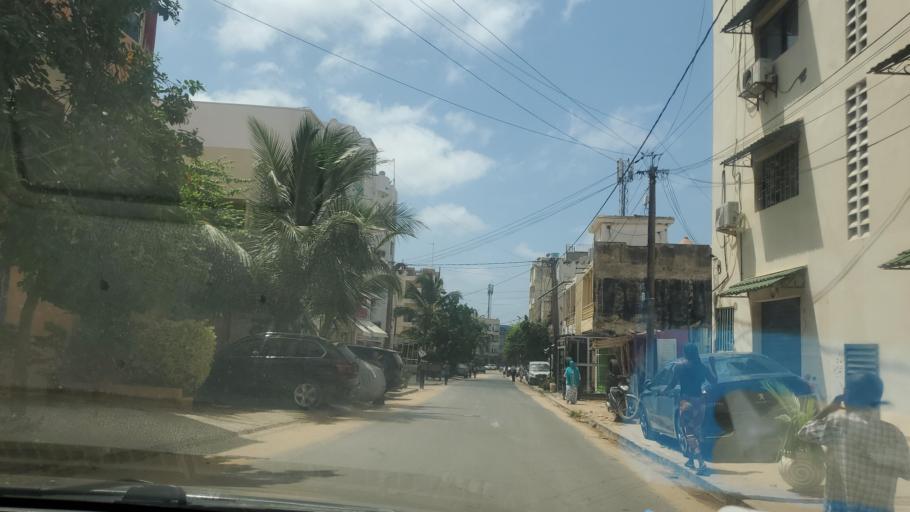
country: SN
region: Dakar
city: Grand Dakar
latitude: 14.7310
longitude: -17.4697
